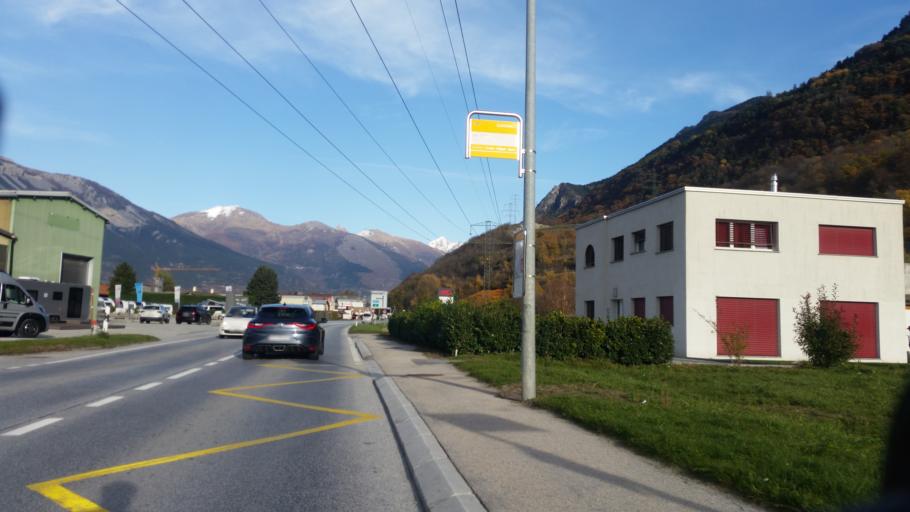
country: CH
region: Valais
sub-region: Sierre District
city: Chalais
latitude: 46.2704
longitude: 7.5169
